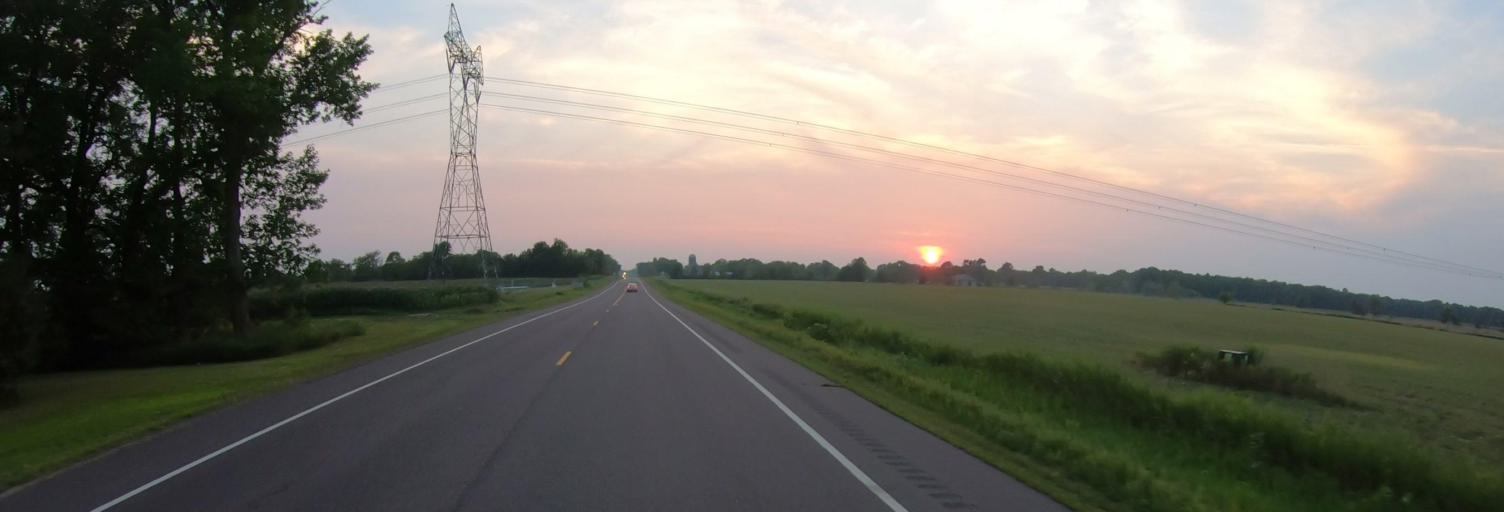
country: US
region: Minnesota
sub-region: Pine County
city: Rock Creek
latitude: 45.7735
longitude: -92.9076
